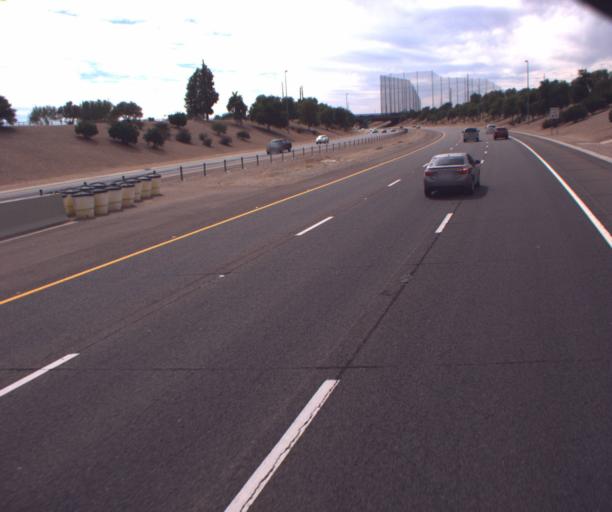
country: US
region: Arizona
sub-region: Maricopa County
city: Gilbert
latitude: 33.3256
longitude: -111.7344
